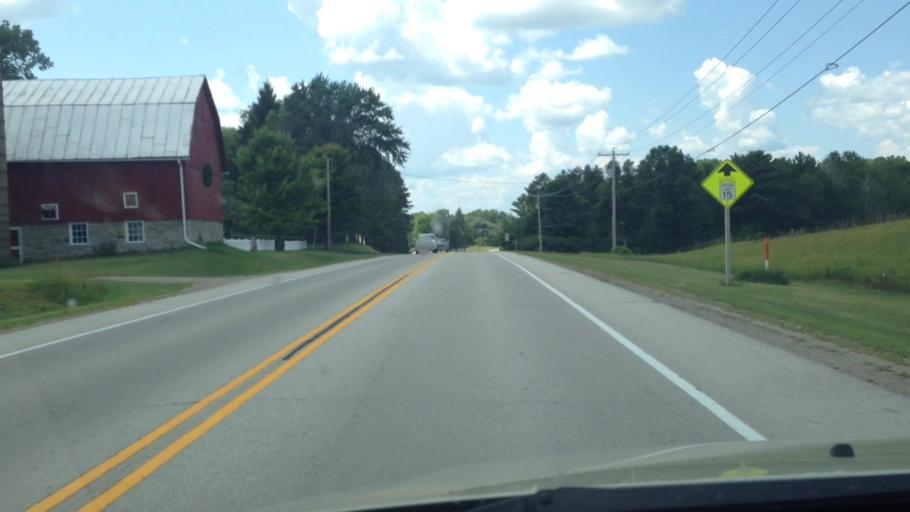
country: US
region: Wisconsin
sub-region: Brown County
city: Suamico
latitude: 44.6363
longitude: -88.0625
